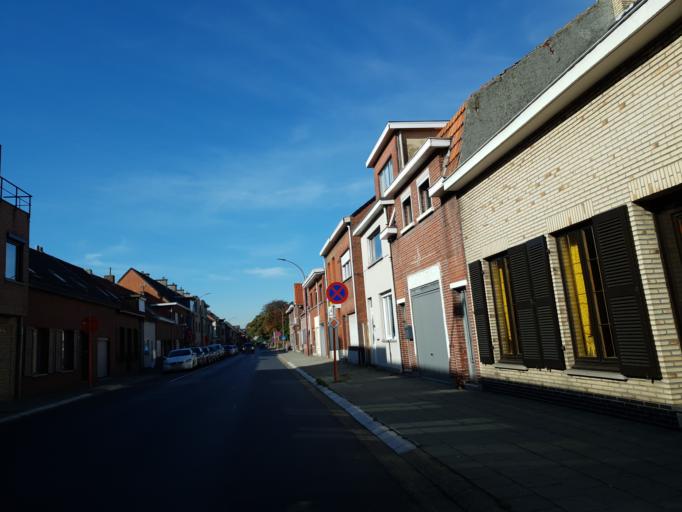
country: BE
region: Flanders
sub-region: Provincie Antwerpen
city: Stabroek
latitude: 51.3327
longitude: 4.3764
